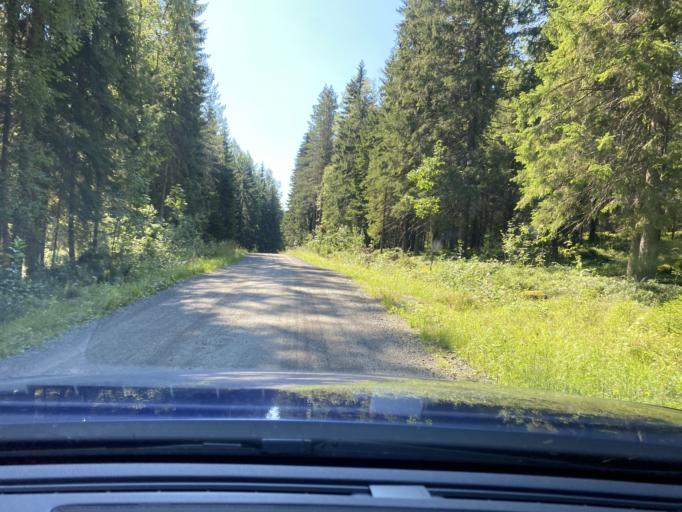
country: FI
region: Central Finland
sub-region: Jaemsae
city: Jaemsae
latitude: 61.8362
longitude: 25.3705
